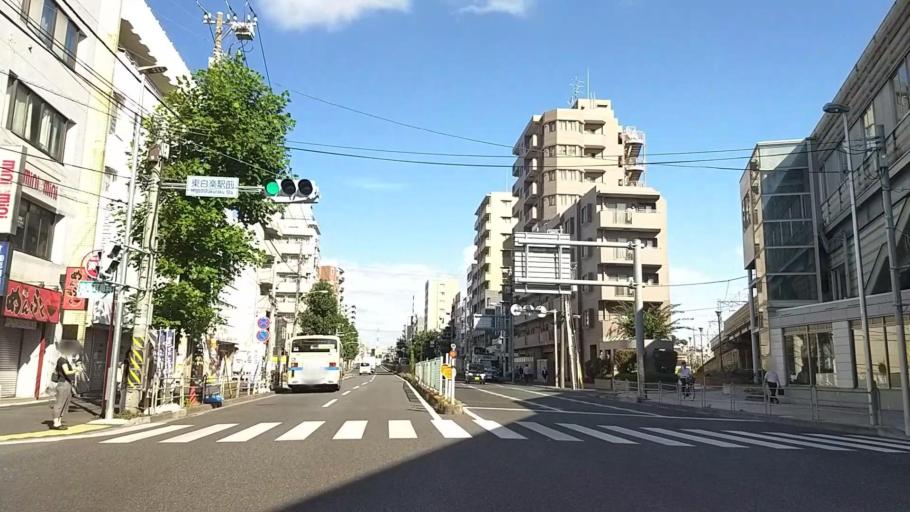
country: JP
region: Kanagawa
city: Yokohama
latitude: 35.4829
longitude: 139.6294
